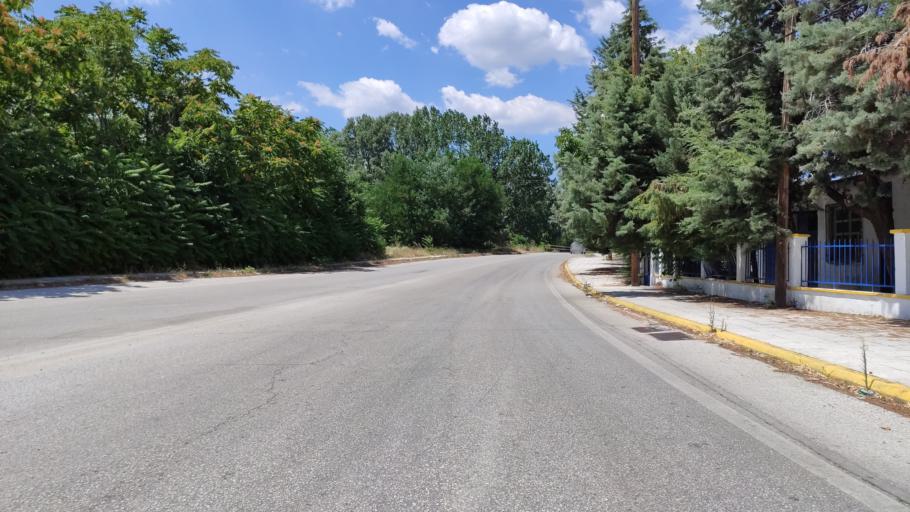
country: GR
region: East Macedonia and Thrace
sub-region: Nomos Rodopis
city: Komotini
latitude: 41.1266
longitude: 25.3863
